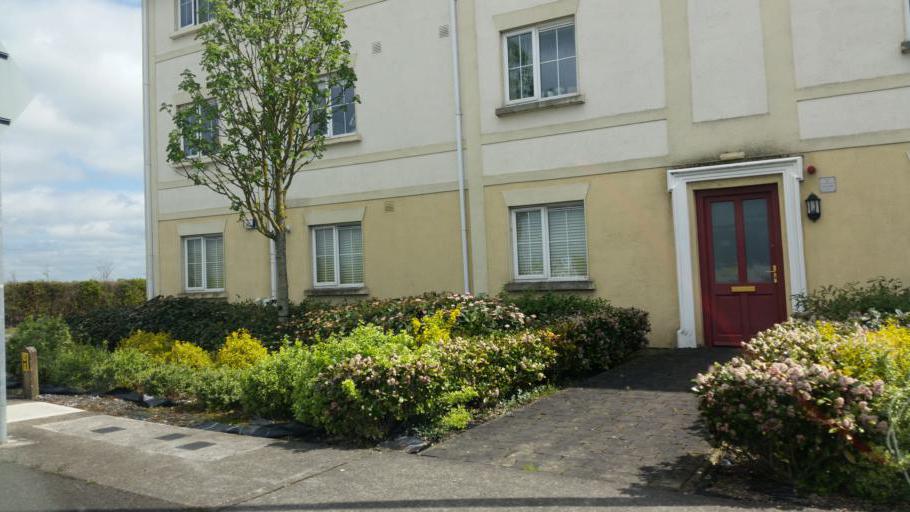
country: IE
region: Leinster
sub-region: Laois
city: Portlaoise
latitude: 53.0505
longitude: -7.3200
